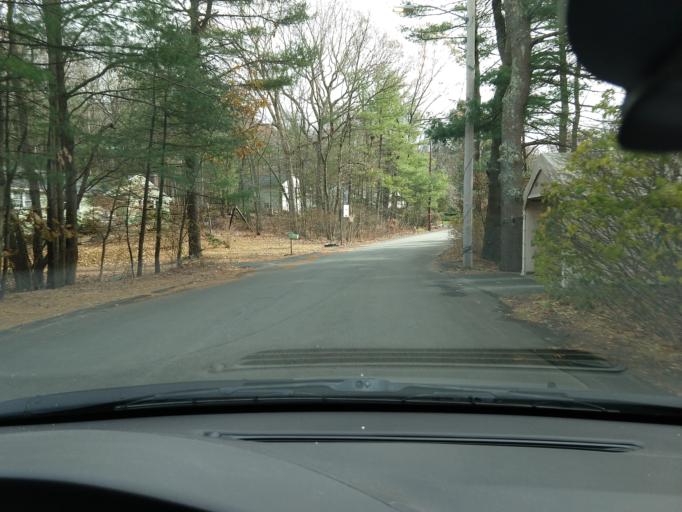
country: US
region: Massachusetts
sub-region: Middlesex County
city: Bedford
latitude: 42.4942
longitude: -71.2502
